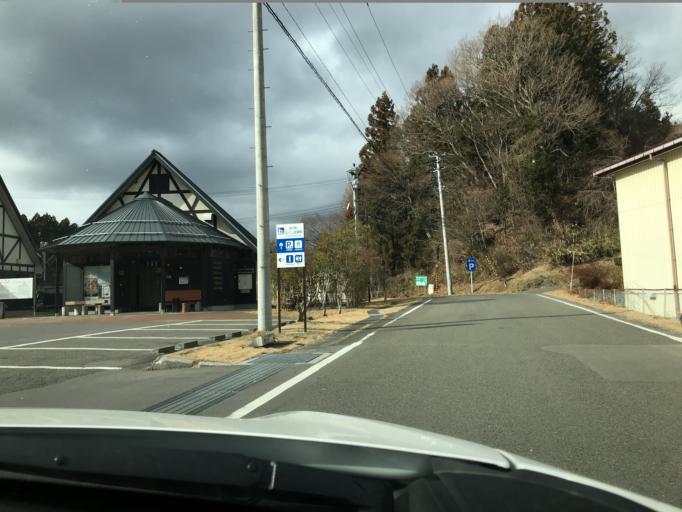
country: JP
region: Fukushima
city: Funehikimachi-funehiki
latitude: 37.5703
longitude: 140.5781
